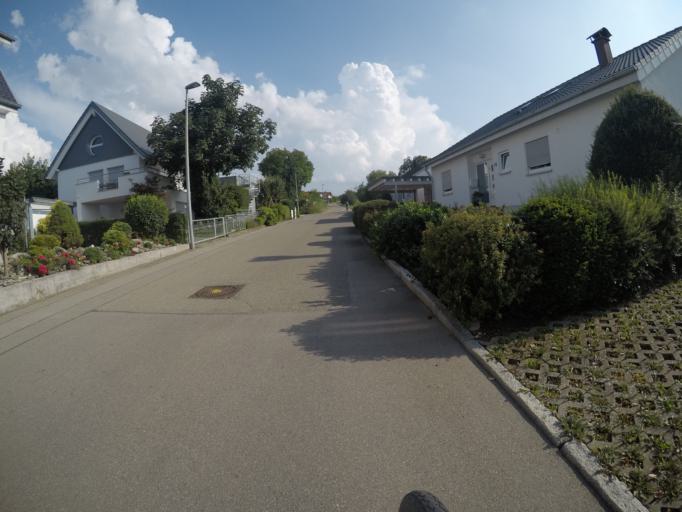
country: DE
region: Baden-Wuerttemberg
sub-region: Tuebingen Region
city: Pliezhausen
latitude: 48.5604
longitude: 9.2314
